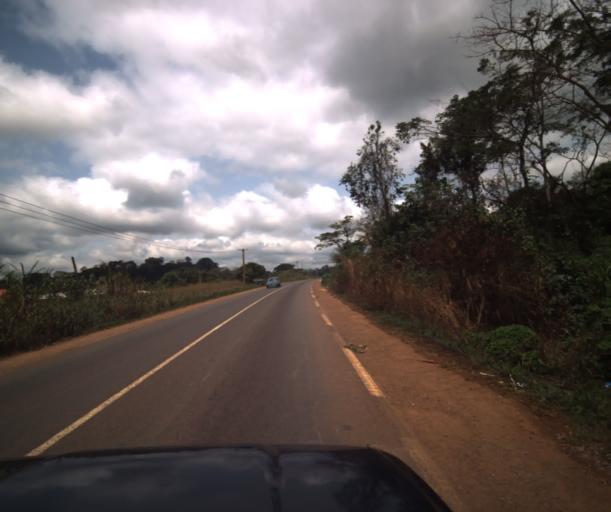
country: CM
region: Centre
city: Mbankomo
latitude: 3.7861
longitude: 11.4480
